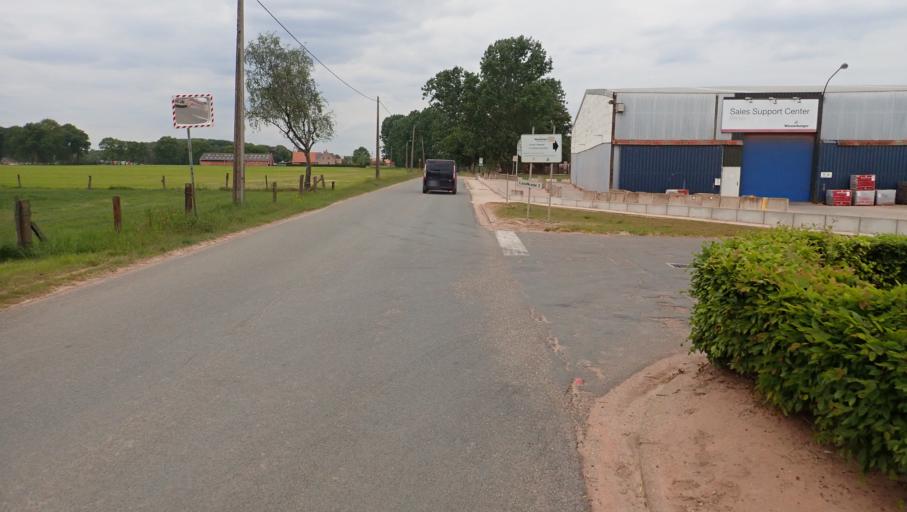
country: BE
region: Flanders
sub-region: Provincie Antwerpen
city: Brecht
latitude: 51.3024
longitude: 4.6676
